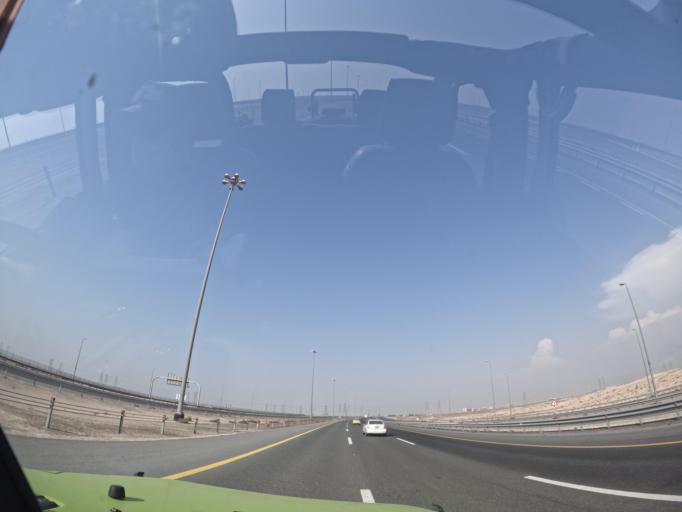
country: AE
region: Dubai
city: Dubai
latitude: 24.8607
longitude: 55.0146
